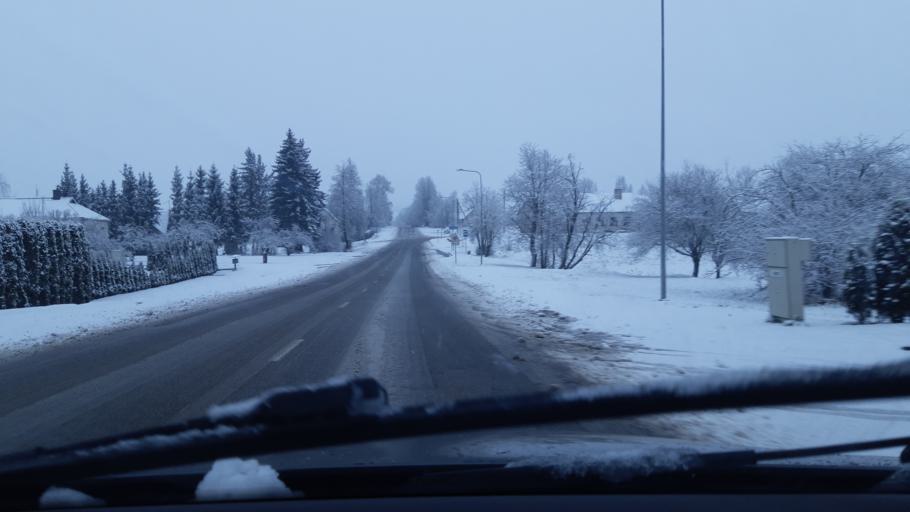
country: LT
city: Kaisiadorys
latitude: 54.8485
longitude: 24.3413
